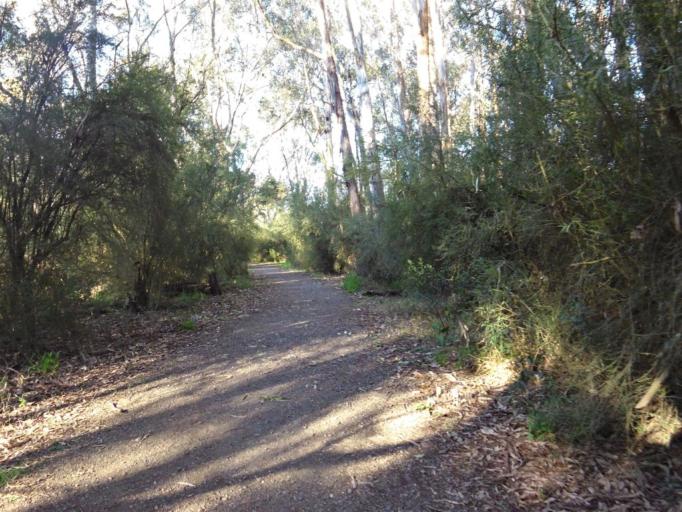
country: AU
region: Victoria
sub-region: Murrindindi
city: Alexandra
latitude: -37.2100
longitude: 145.4278
